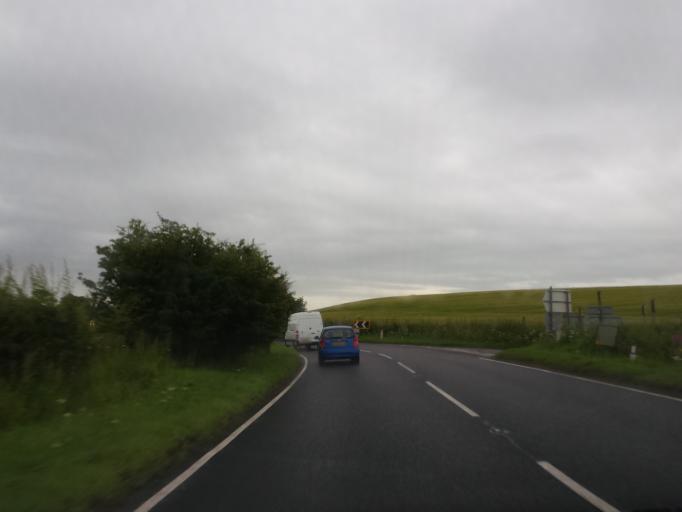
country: GB
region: Scotland
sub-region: Fife
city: Balmullo
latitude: 56.3992
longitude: -2.9113
